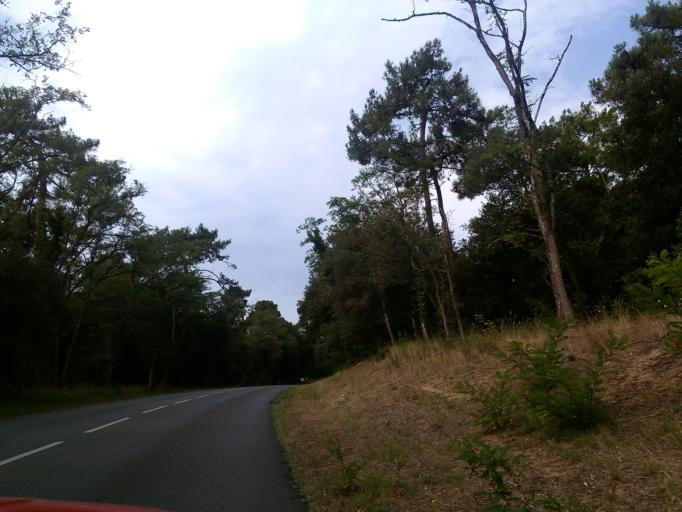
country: FR
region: Poitou-Charentes
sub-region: Departement de la Charente-Maritime
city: La Tremblade
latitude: 45.7888
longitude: -1.1874
